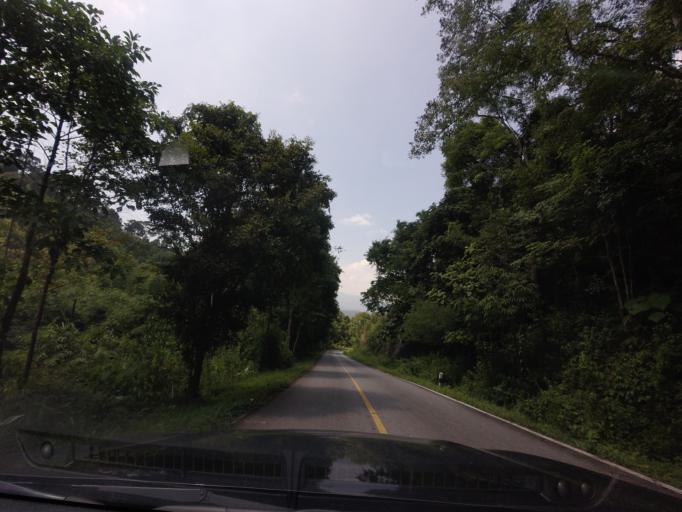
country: TH
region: Loei
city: Na Haeo
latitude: 17.6292
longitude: 100.9046
